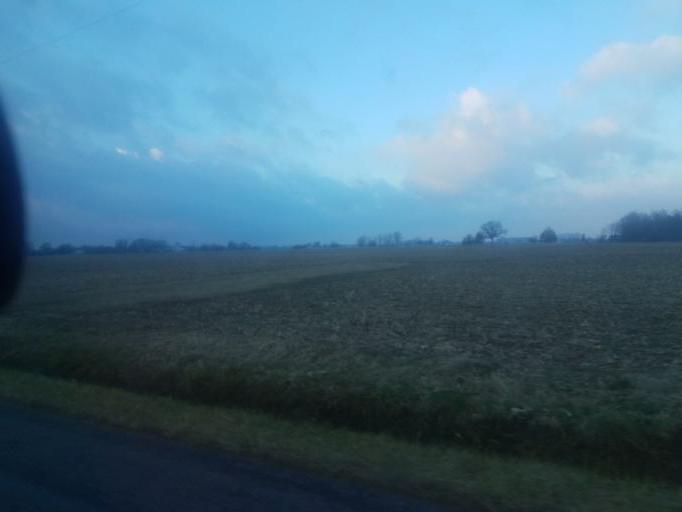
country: US
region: Ohio
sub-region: Marion County
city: Marion
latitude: 40.6352
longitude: -83.1889
